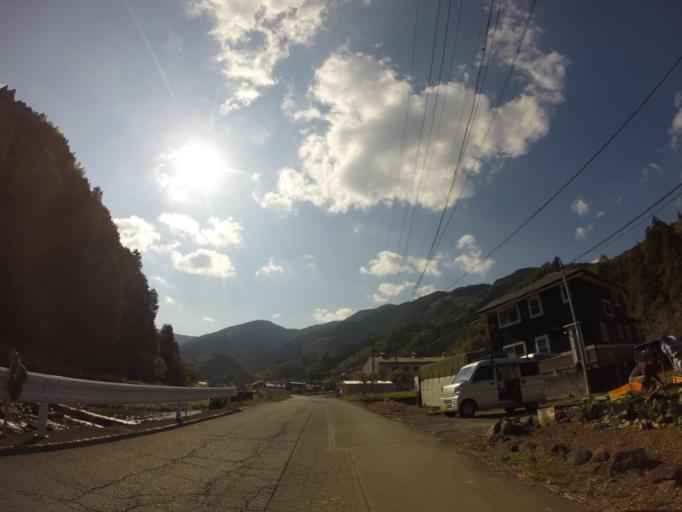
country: JP
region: Shizuoka
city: Shizuoka-shi
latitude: 35.1117
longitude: 138.4502
